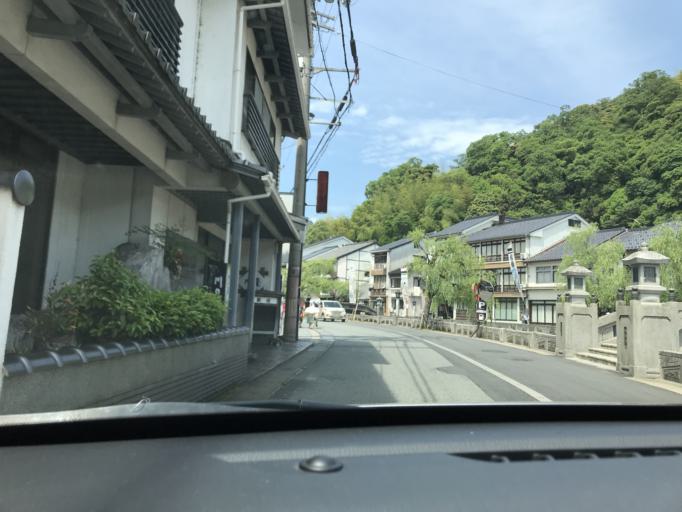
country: JP
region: Hyogo
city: Toyooka
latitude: 35.6264
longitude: 134.8112
